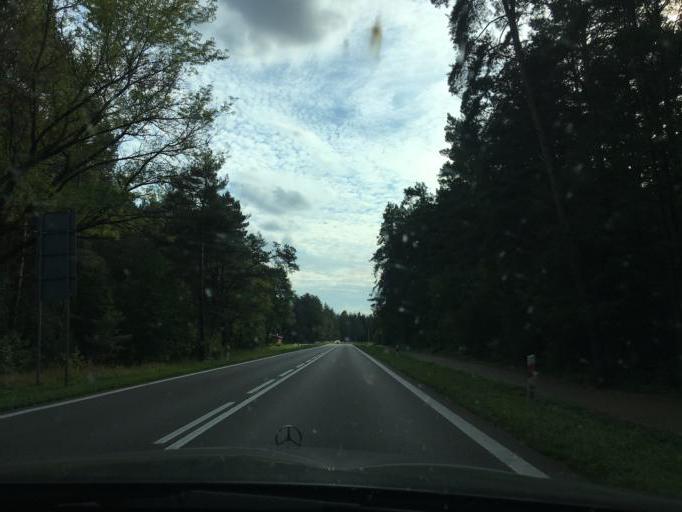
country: PL
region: Podlasie
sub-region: Powiat grajewski
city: Rajgrod
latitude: 53.7108
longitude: 22.6715
